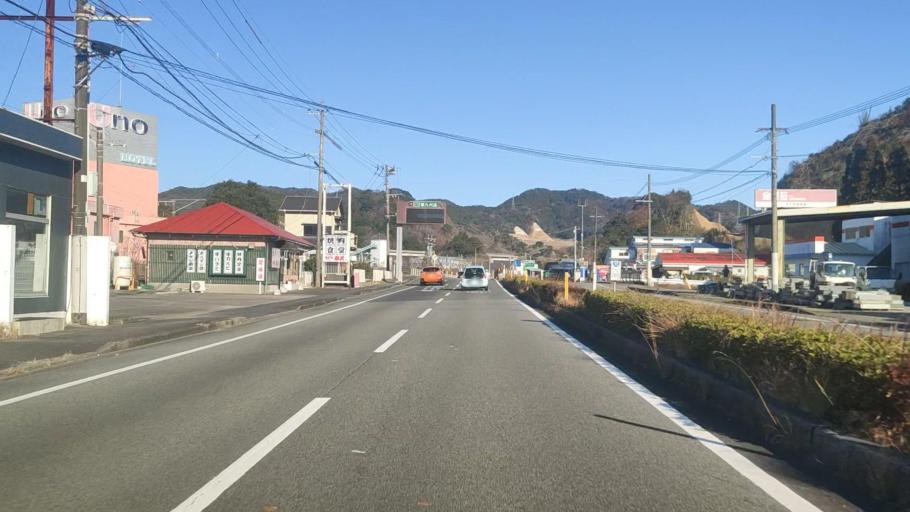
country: JP
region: Miyazaki
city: Nobeoka
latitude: 32.4941
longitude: 131.6629
